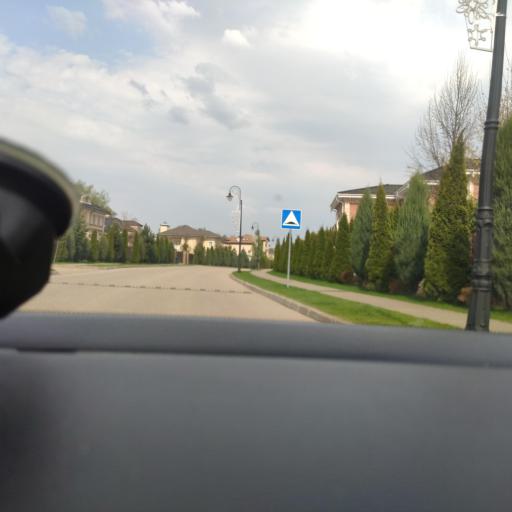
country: RU
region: Moskovskaya
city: Nakhabino
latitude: 55.8229
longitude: 37.1390
